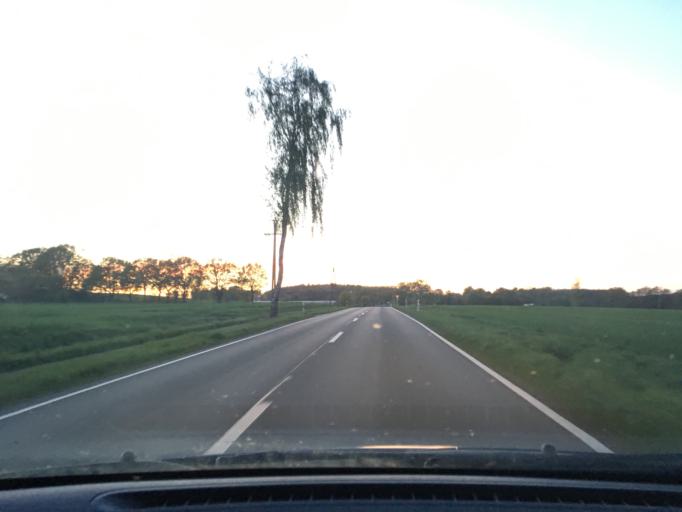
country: DE
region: Lower Saxony
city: Salzhausen
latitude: 53.2143
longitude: 10.1849
